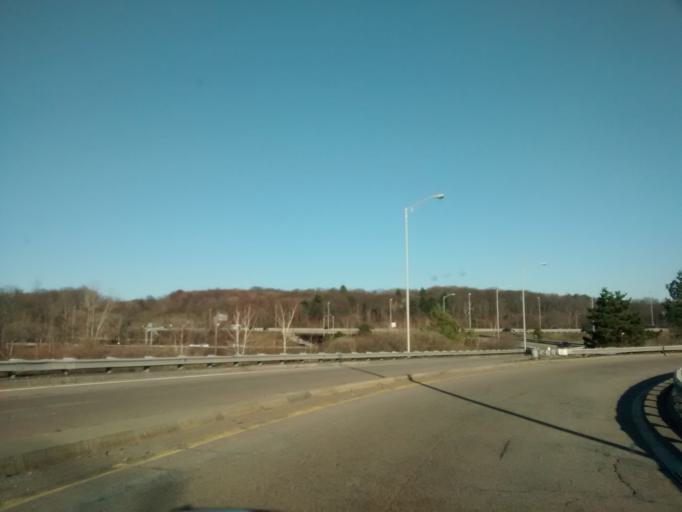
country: US
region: Massachusetts
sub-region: Worcester County
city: Millbury
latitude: 42.2091
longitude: -71.7869
